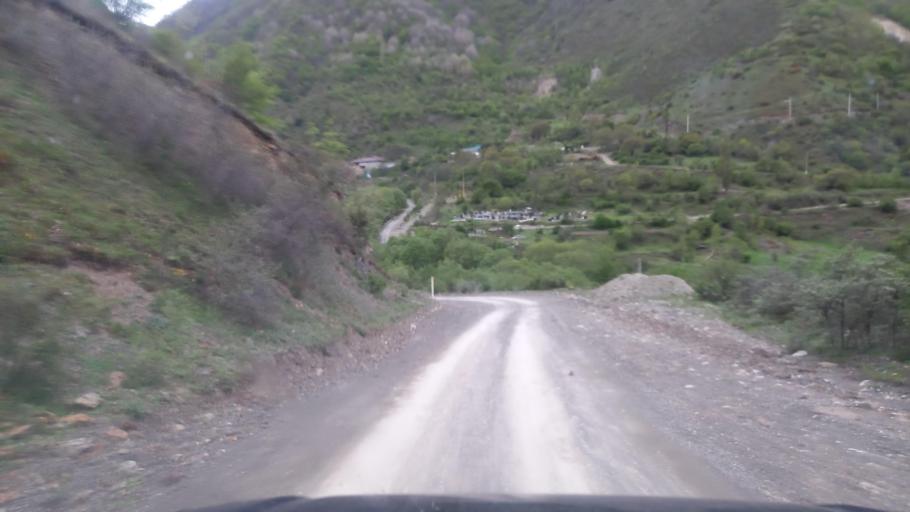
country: RU
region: North Ossetia
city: Mizur
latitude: 42.8505
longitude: 44.1577
